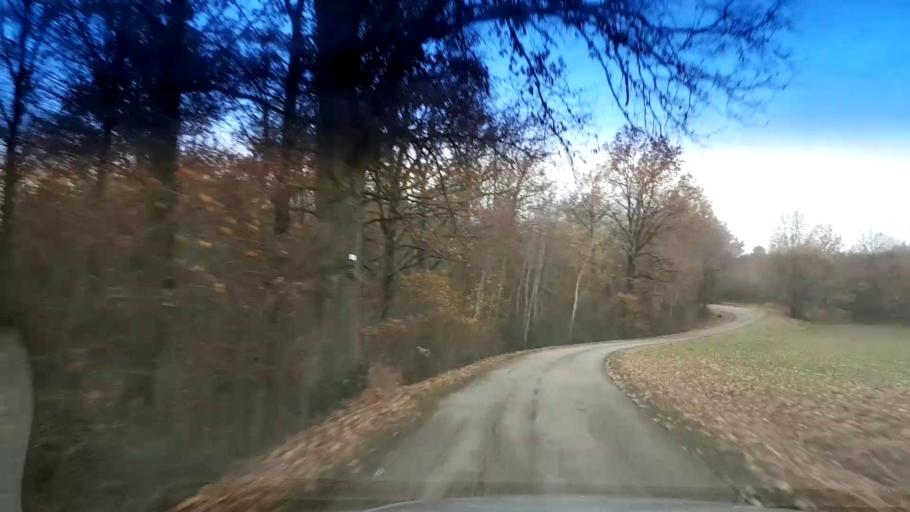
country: DE
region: Bavaria
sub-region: Upper Franconia
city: Zapfendorf
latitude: 49.9977
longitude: 10.9445
